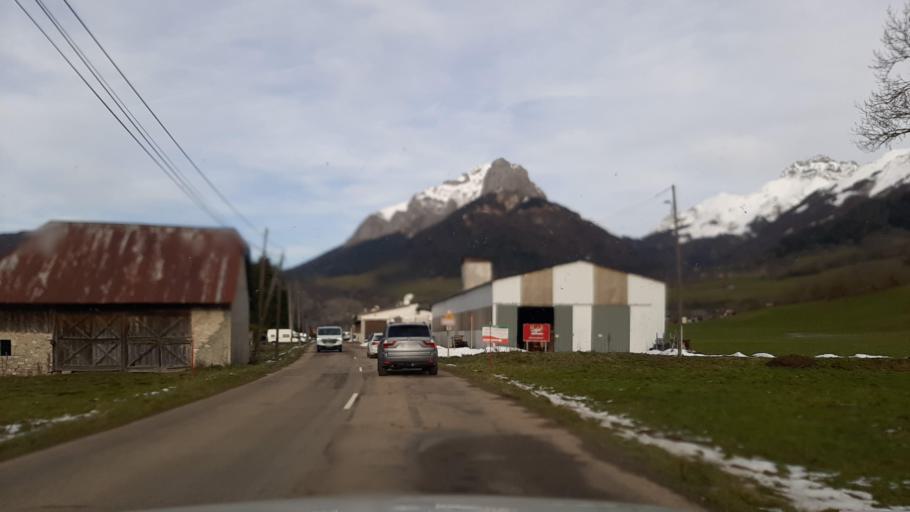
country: FR
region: Rhone-Alpes
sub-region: Departement de la Savoie
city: Gresy-sur-Isere
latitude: 45.6443
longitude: 6.1647
